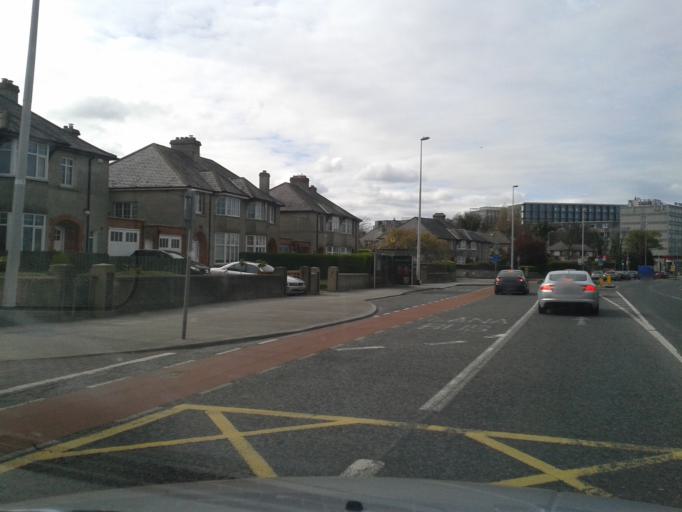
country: IE
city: Booterstown
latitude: 53.3106
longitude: -6.1994
